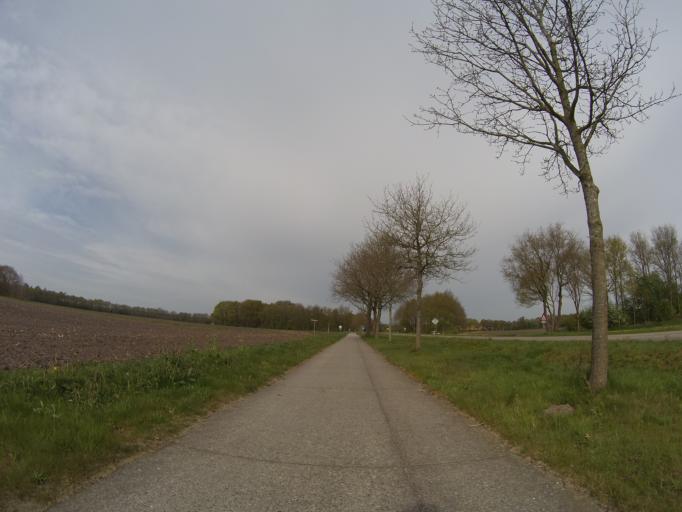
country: NL
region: Drenthe
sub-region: Gemeente Borger-Odoorn
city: Borger
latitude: 52.8392
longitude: 6.6662
